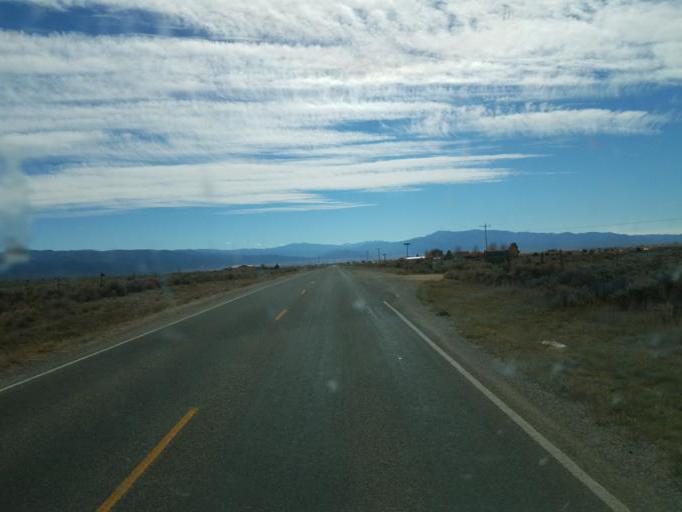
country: US
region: New Mexico
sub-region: Taos County
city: Arroyo Seco
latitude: 36.4897
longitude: -105.5937
